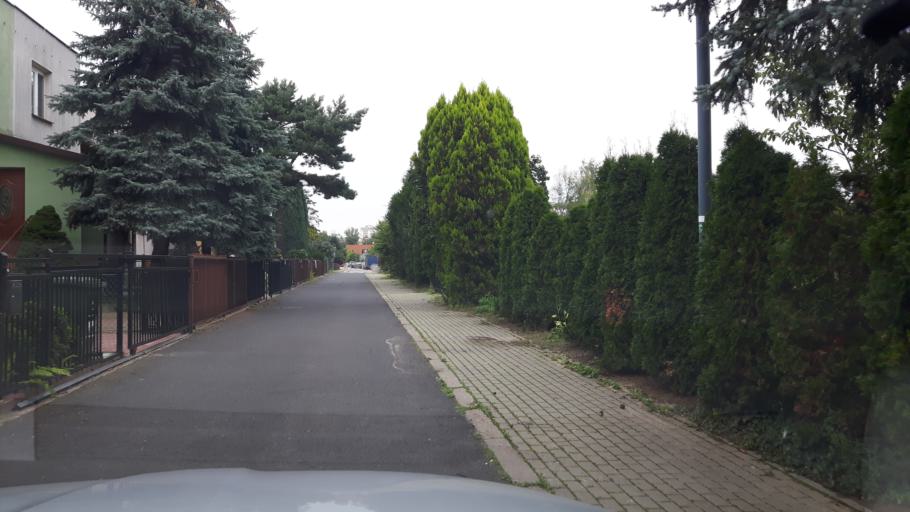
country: PL
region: Masovian Voivodeship
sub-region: Warszawa
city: Targowek
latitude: 52.2832
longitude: 21.0580
